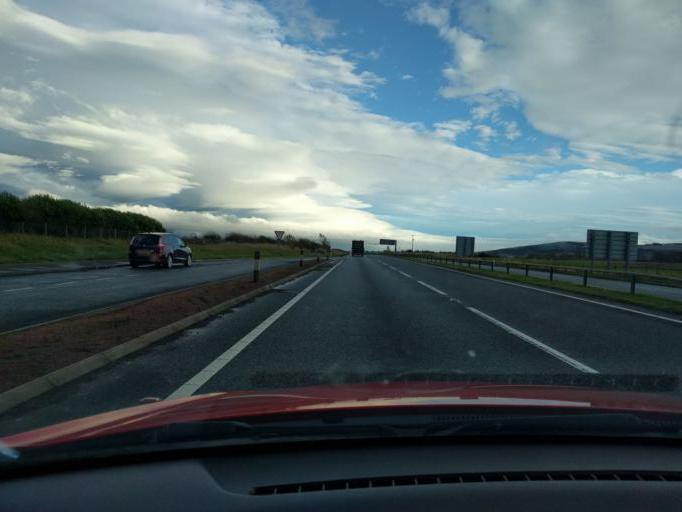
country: GB
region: Scotland
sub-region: East Lothian
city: Dunbar
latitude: 55.9887
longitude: -2.5538
